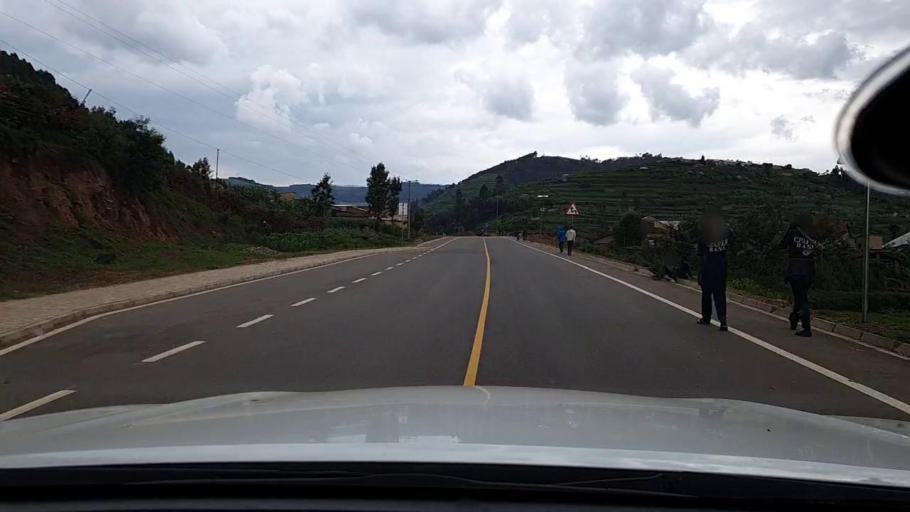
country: RW
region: Northern Province
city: Byumba
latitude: -1.6362
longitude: 29.9279
